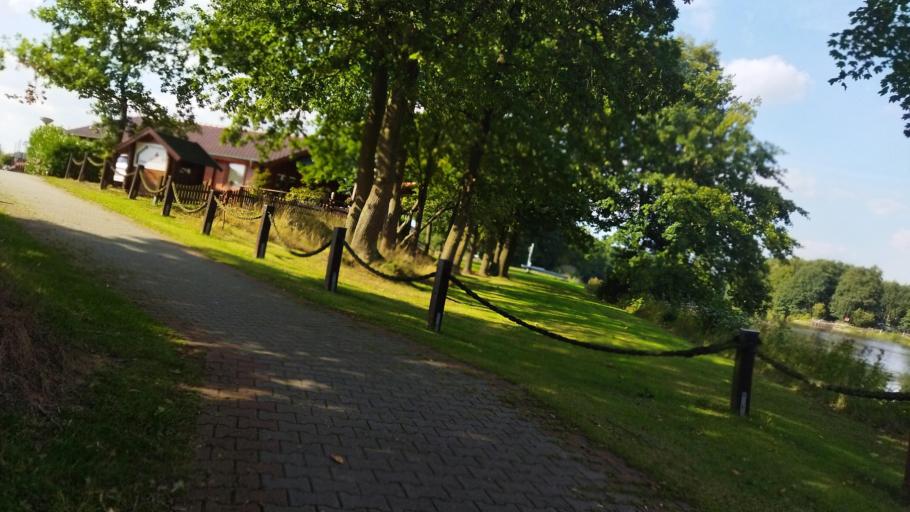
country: DE
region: Lower Saxony
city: Walchum
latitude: 52.9289
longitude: 7.2937
